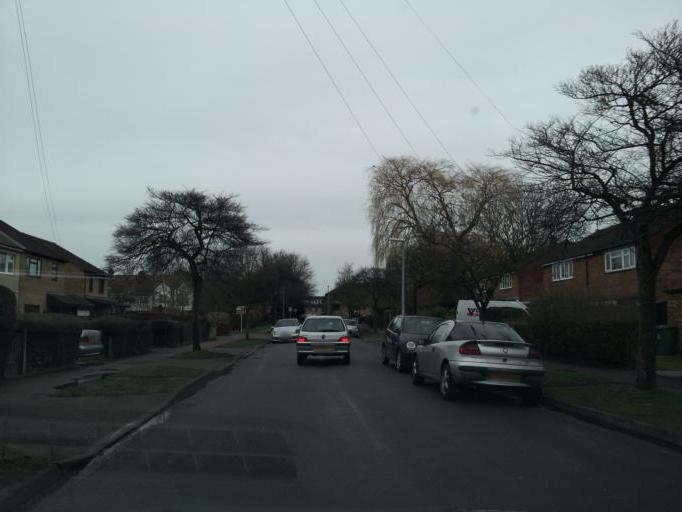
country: GB
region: England
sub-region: Cambridgeshire
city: Cambridge
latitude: 52.1854
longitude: 0.1541
